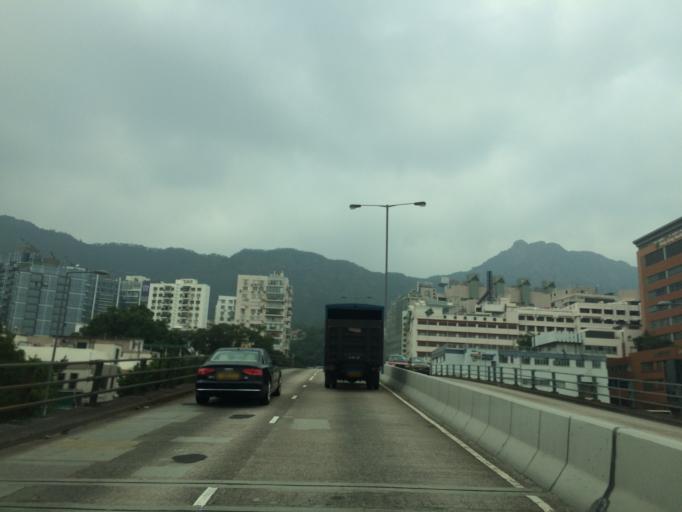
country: HK
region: Wong Tai Sin
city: Wong Tai Sin
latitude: 22.3381
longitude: 114.1791
